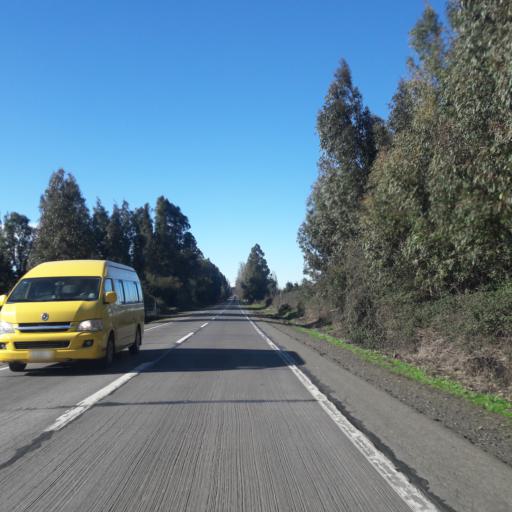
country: CL
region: Araucania
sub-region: Provincia de Malleco
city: Angol
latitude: -37.7565
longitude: -72.5775
